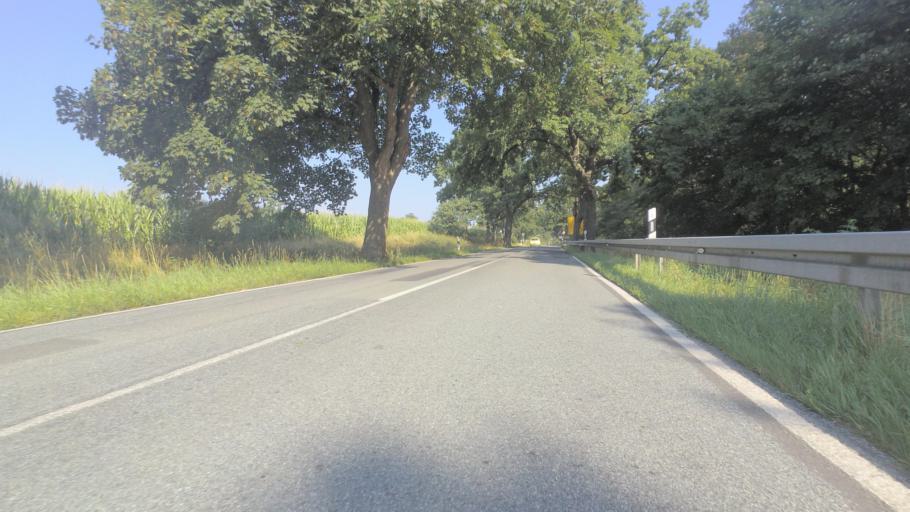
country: DE
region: Mecklenburg-Vorpommern
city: Grabowhofe
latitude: 53.6063
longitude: 12.4682
